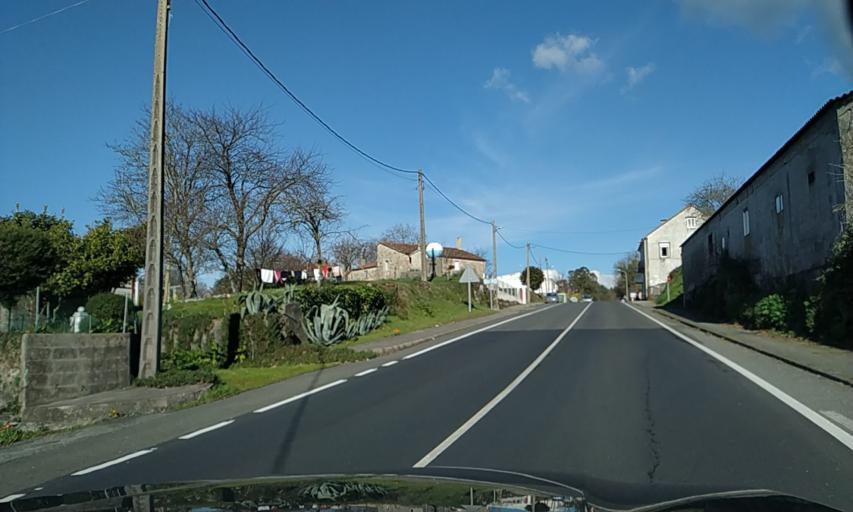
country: ES
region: Galicia
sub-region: Provincia da Coruna
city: Ribeira
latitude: 42.7057
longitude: -8.3985
